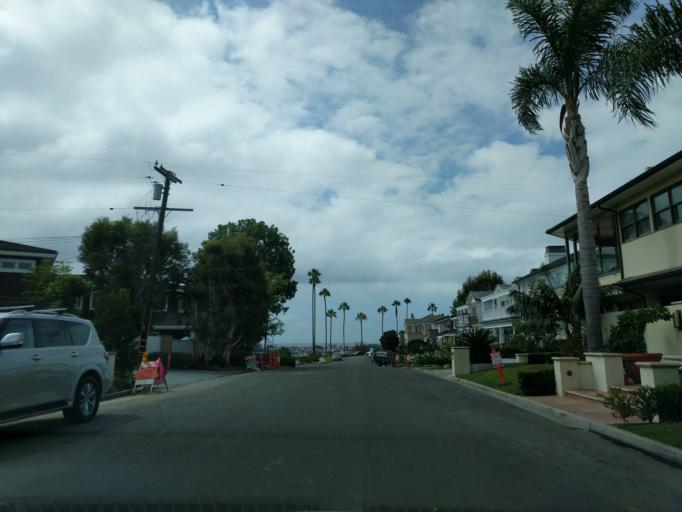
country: US
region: California
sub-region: Orange County
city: Newport Beach
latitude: 33.6241
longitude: -117.9214
